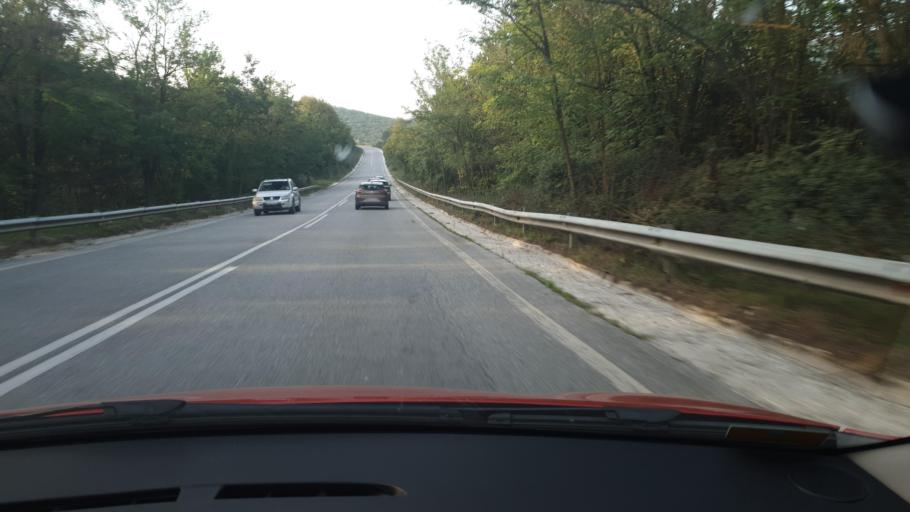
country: GR
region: Central Macedonia
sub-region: Nomos Chalkidikis
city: Polygyros
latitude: 40.4474
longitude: 23.4148
